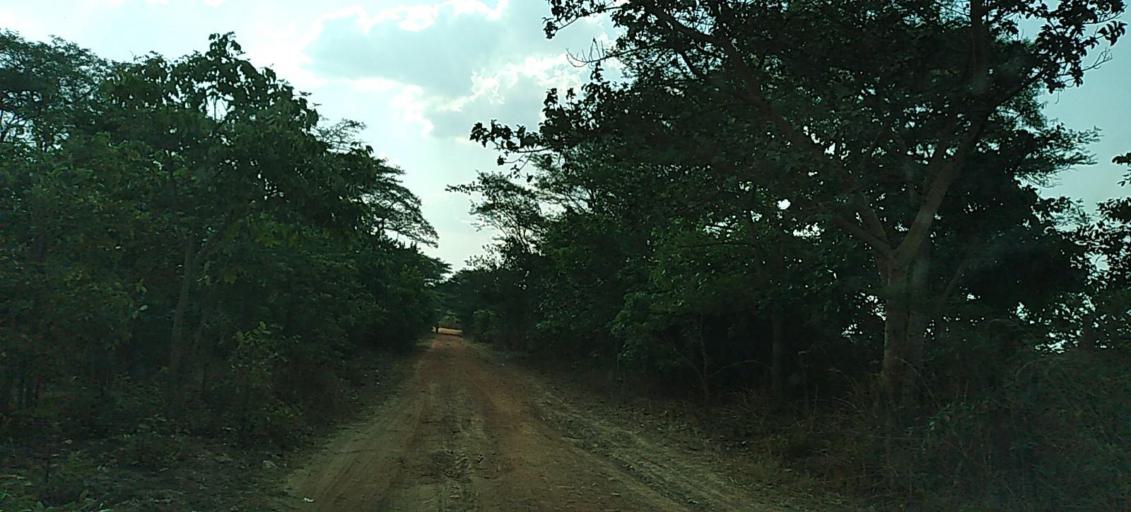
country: ZM
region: Copperbelt
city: Mpongwe
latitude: -13.4759
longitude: 28.0801
